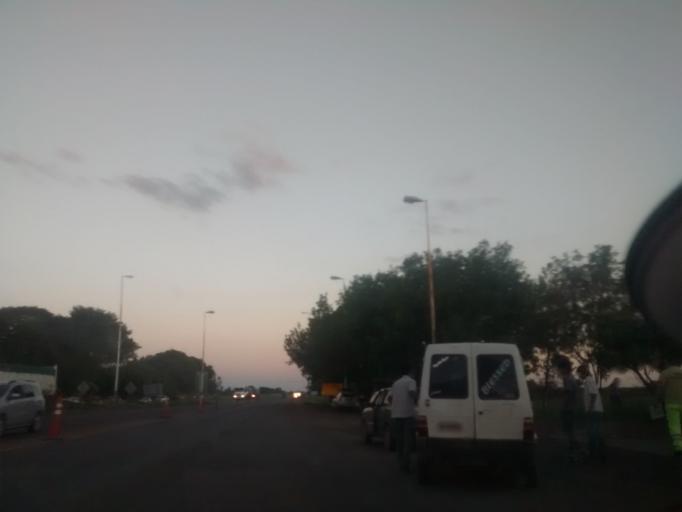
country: AR
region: Chaco
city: Makalle
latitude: -27.1869
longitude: -59.3262
